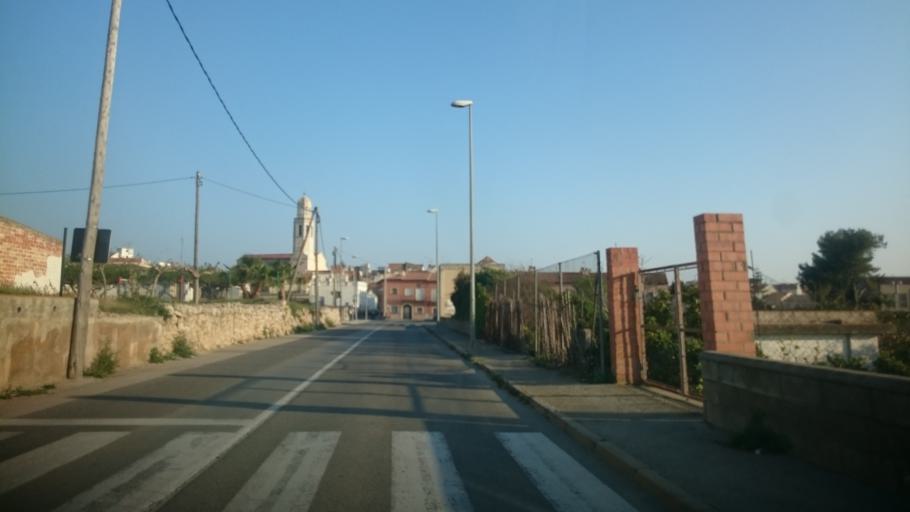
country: ES
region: Catalonia
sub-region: Provincia de Barcelona
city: Cubelles
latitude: 41.2101
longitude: 1.6707
